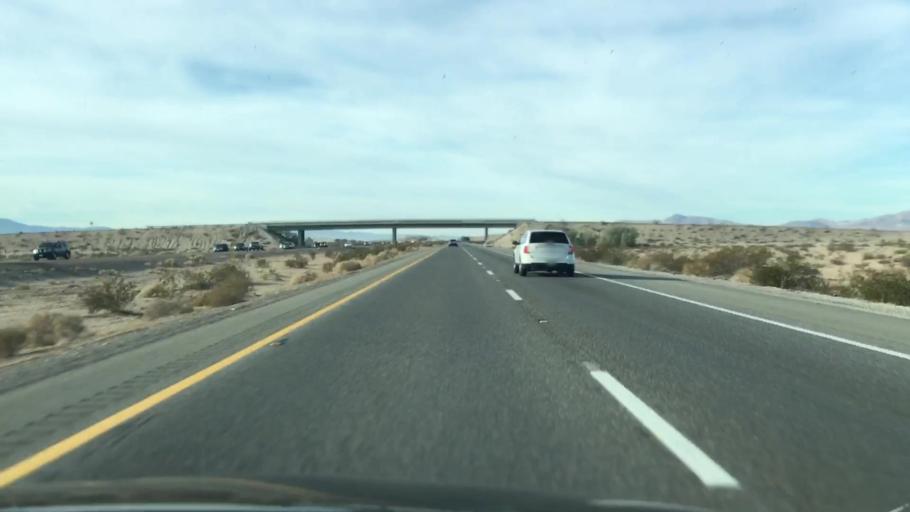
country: US
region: California
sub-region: San Bernardino County
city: Fort Irwin
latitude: 34.9858
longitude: -116.5945
